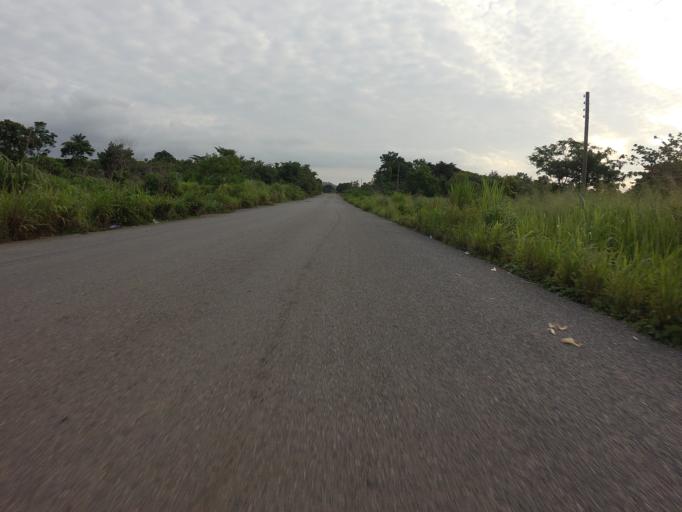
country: GH
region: Volta
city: Kpandu
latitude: 6.8666
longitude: 0.4027
